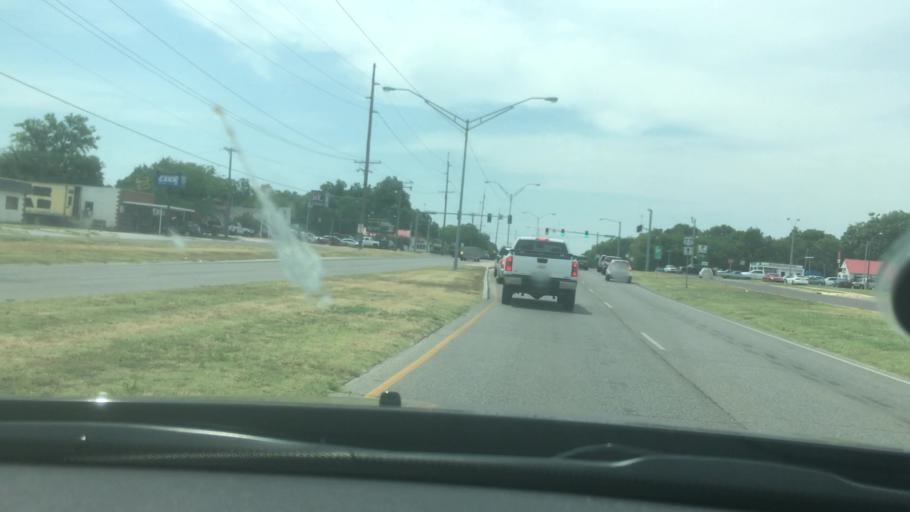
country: US
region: Oklahoma
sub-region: Carter County
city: Ardmore
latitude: 34.1759
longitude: -97.1434
